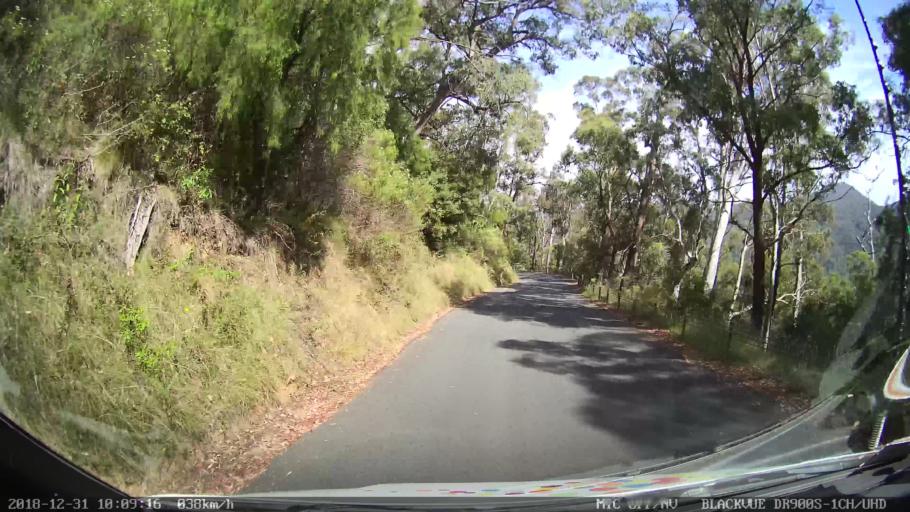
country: AU
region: New South Wales
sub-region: Snowy River
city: Jindabyne
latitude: -36.5363
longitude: 148.1764
